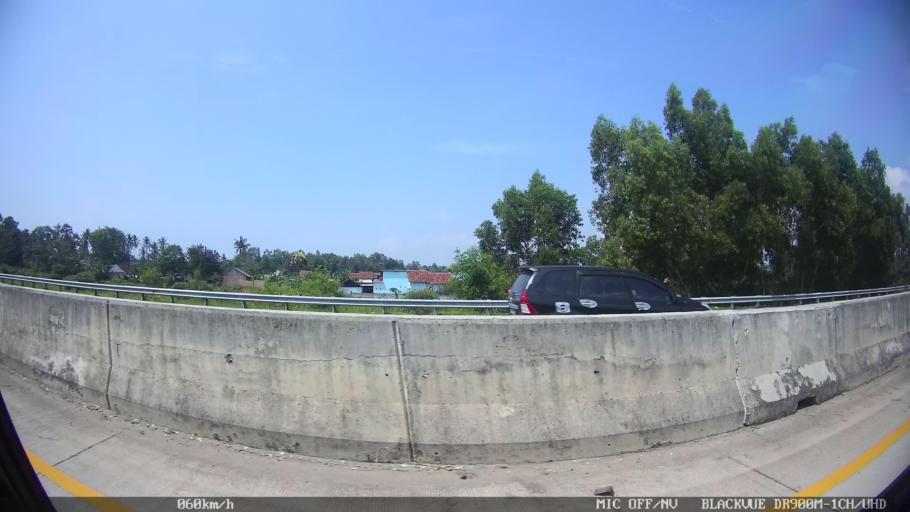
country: ID
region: Lampung
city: Kedaton
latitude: -5.3285
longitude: 105.2861
